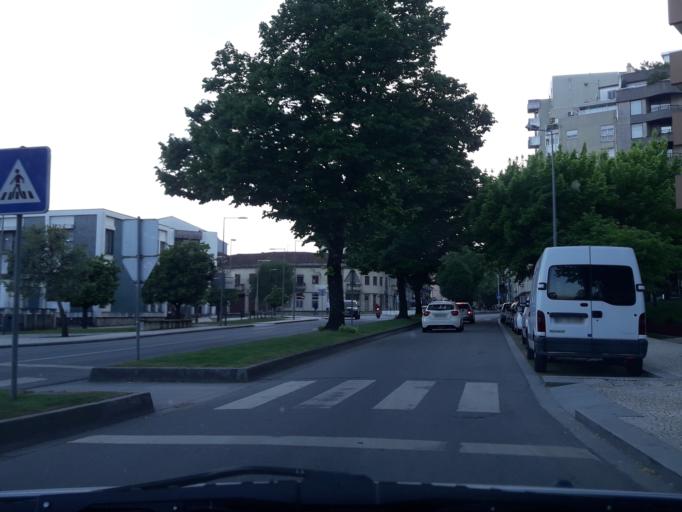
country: PT
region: Braga
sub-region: Vila Nova de Famalicao
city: Vila Nova de Famalicao
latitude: 41.4096
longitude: -8.5170
